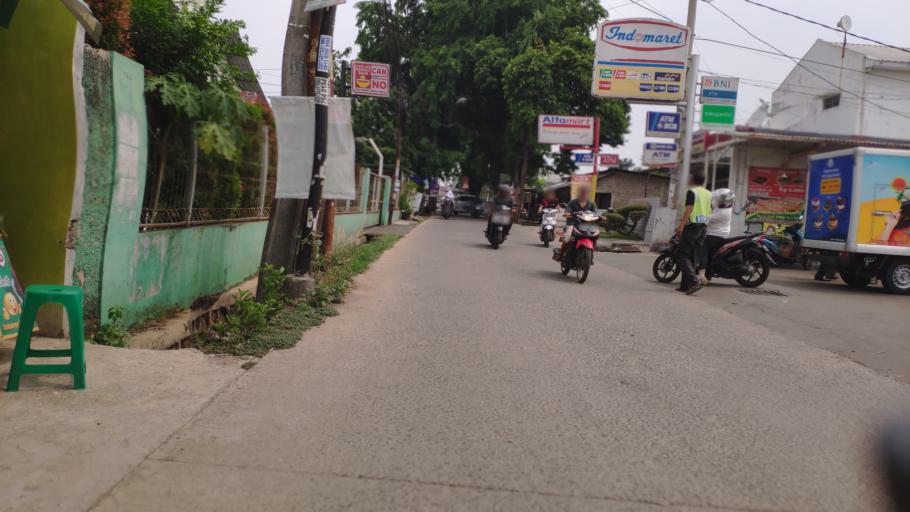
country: ID
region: West Java
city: Depok
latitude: -6.3736
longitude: 106.8009
